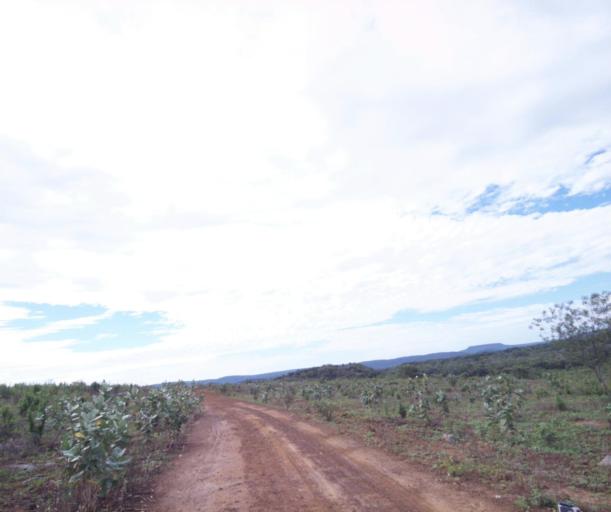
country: BR
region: Bahia
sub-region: Carinhanha
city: Carinhanha
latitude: -14.2317
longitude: -44.4287
